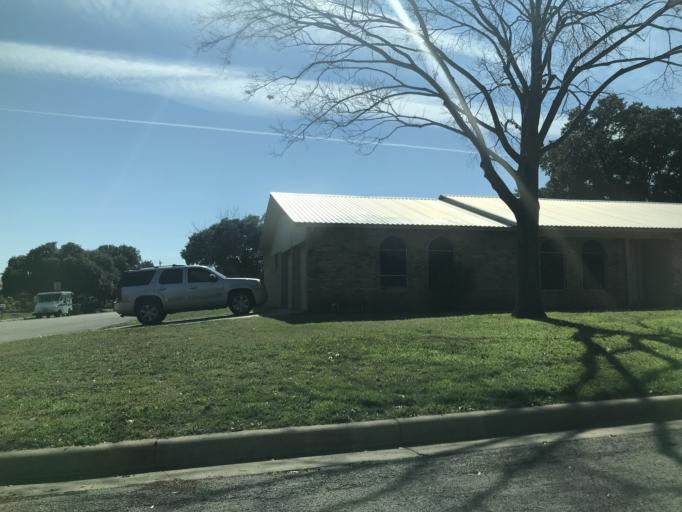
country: US
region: Texas
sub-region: Tom Green County
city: San Angelo
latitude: 31.4318
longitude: -100.4854
